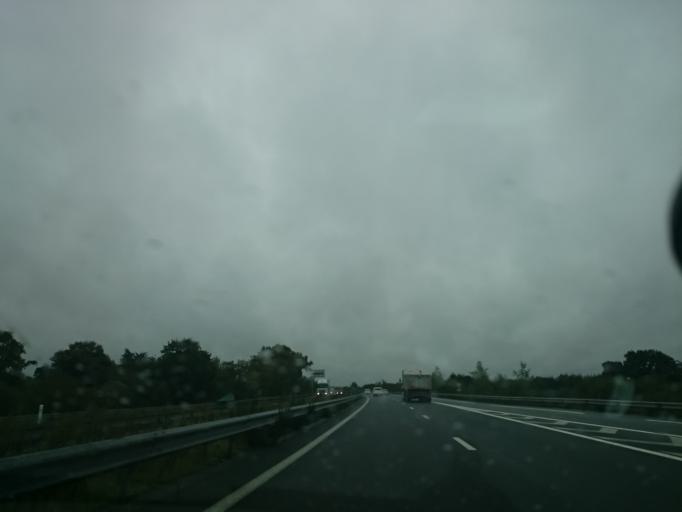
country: FR
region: Brittany
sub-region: Departement du Morbihan
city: Nivillac
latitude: 47.5011
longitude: -2.2638
